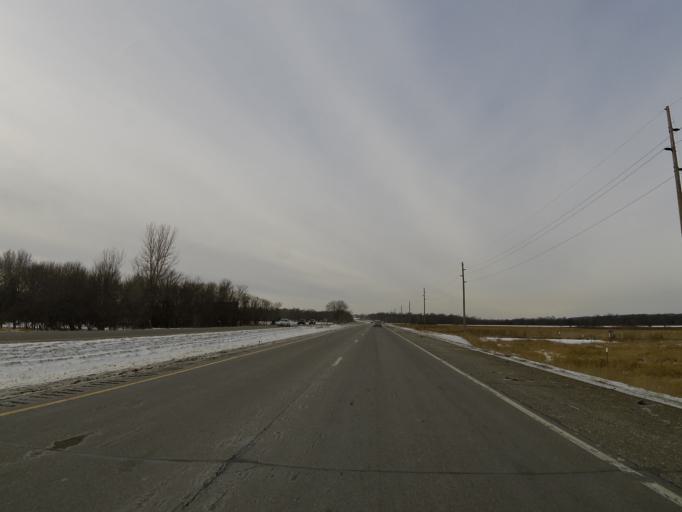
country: US
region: Minnesota
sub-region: Scott County
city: Jordan
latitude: 44.6484
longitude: -93.6987
